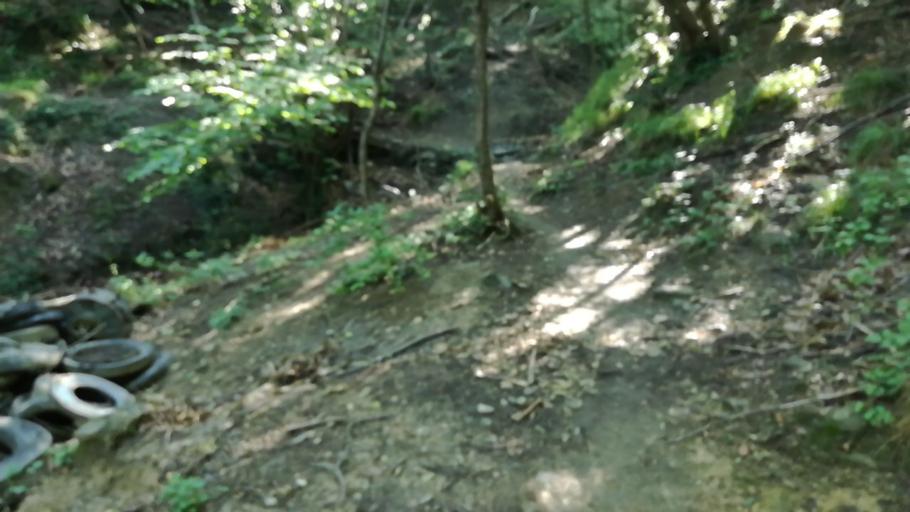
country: IT
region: Liguria
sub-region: Provincia di Genova
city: Genoa
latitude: 44.4283
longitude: 8.9030
